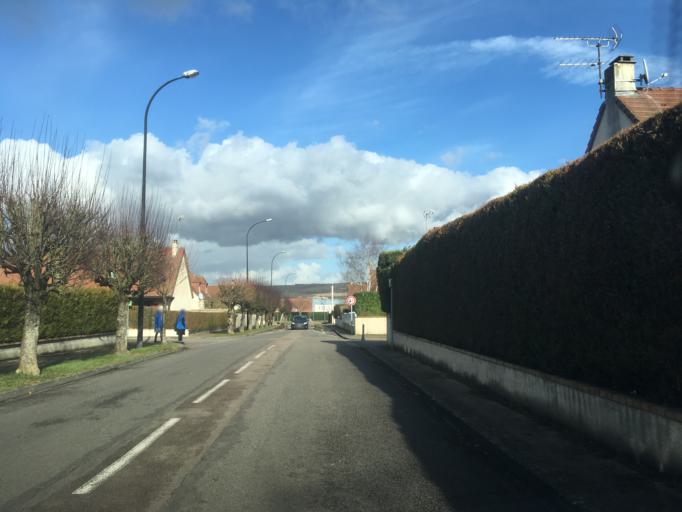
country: FR
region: Haute-Normandie
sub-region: Departement de l'Eure
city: Vernon
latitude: 49.0946
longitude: 1.4588
